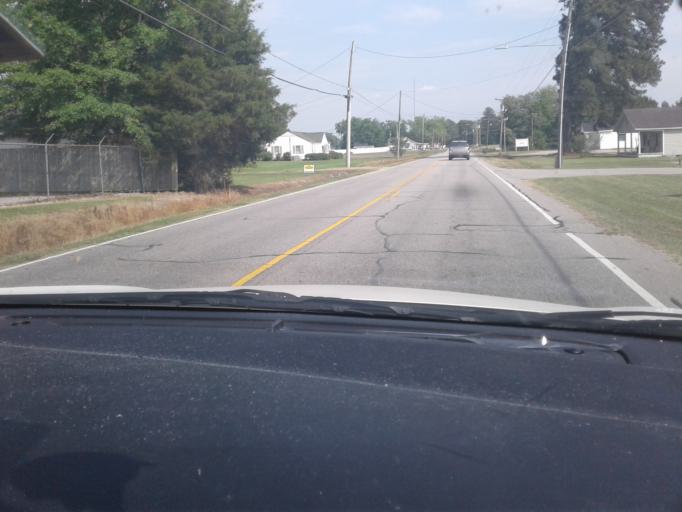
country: US
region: North Carolina
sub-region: Harnett County
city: Erwin
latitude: 35.3214
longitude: -78.6574
